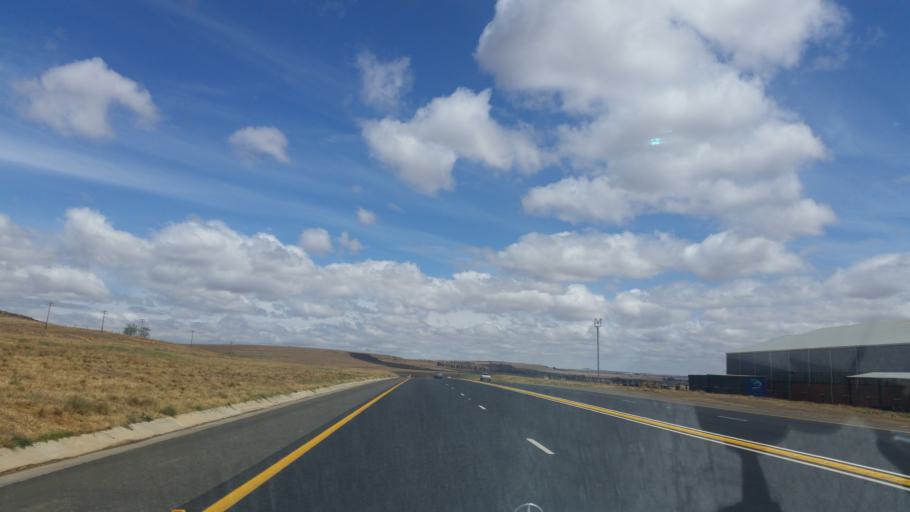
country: ZA
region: Orange Free State
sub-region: Thabo Mofutsanyana District Municipality
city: Harrismith
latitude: -28.2867
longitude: 29.1015
